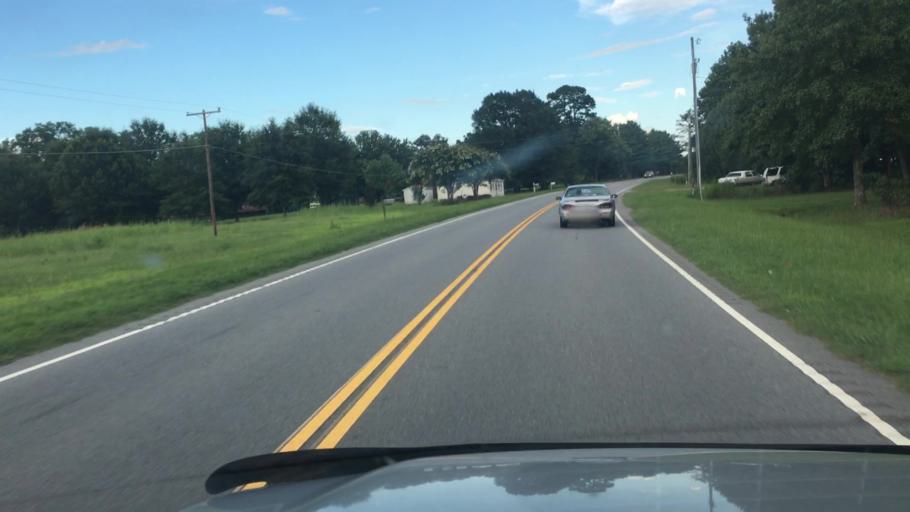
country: US
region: South Carolina
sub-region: Cherokee County
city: Gaffney
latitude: 35.1304
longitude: -81.7461
